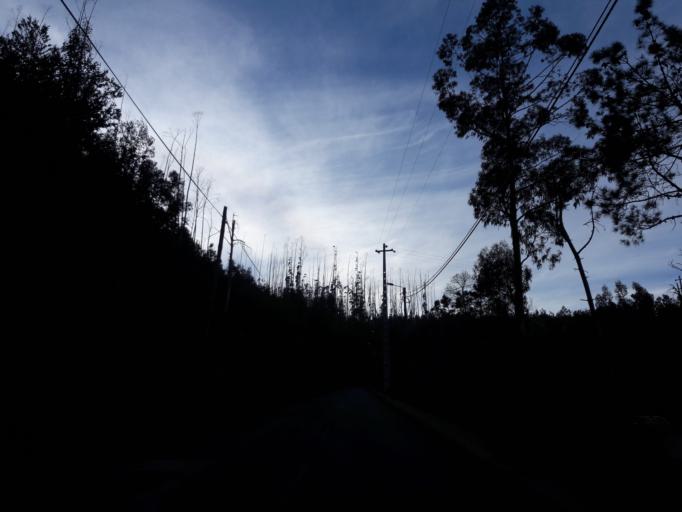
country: PT
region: Madeira
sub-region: Santa Cruz
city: Camacha
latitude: 32.6870
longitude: -16.8618
